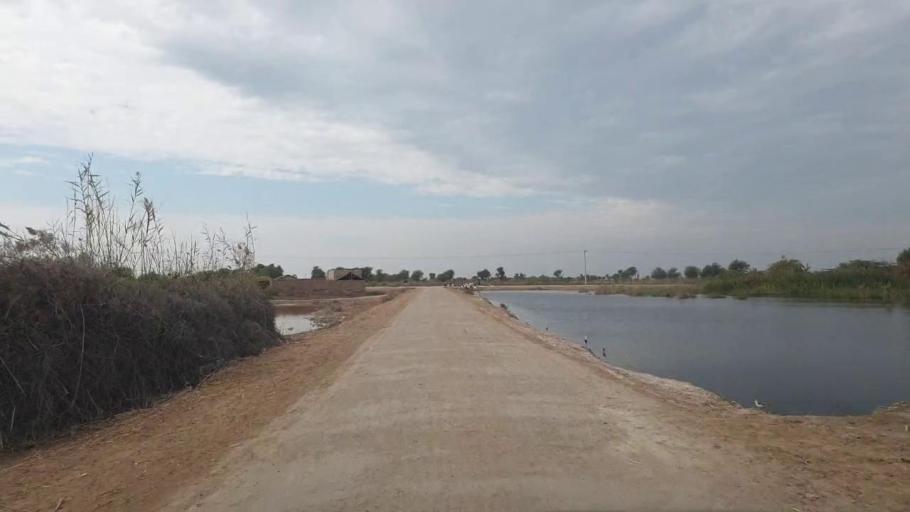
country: PK
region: Sindh
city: Jhol
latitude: 26.0033
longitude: 68.8752
